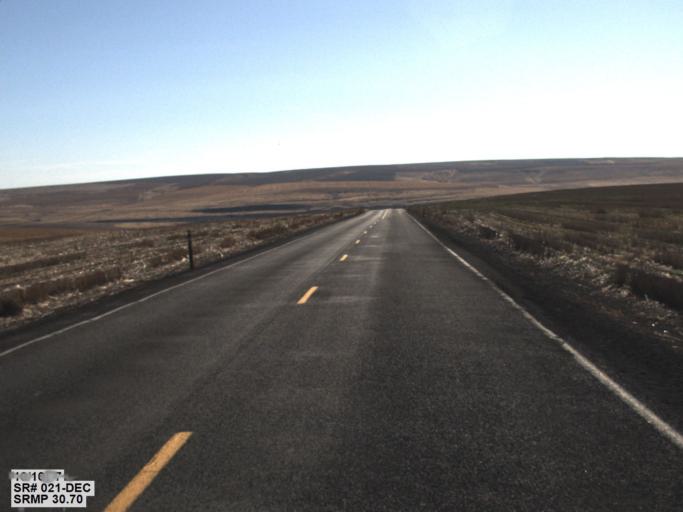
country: US
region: Washington
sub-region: Adams County
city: Ritzville
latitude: 46.9949
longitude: -118.6637
